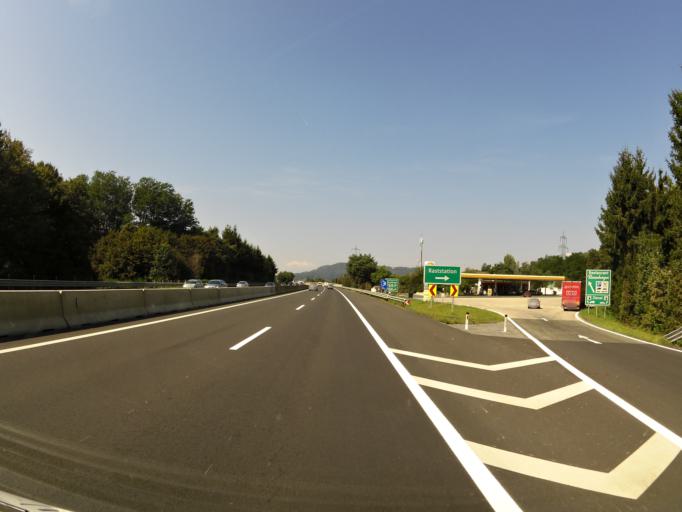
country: AT
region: Styria
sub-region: Politischer Bezirk Leibnitz
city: Kaindorf an der Sulm
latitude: 46.8297
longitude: 15.5534
